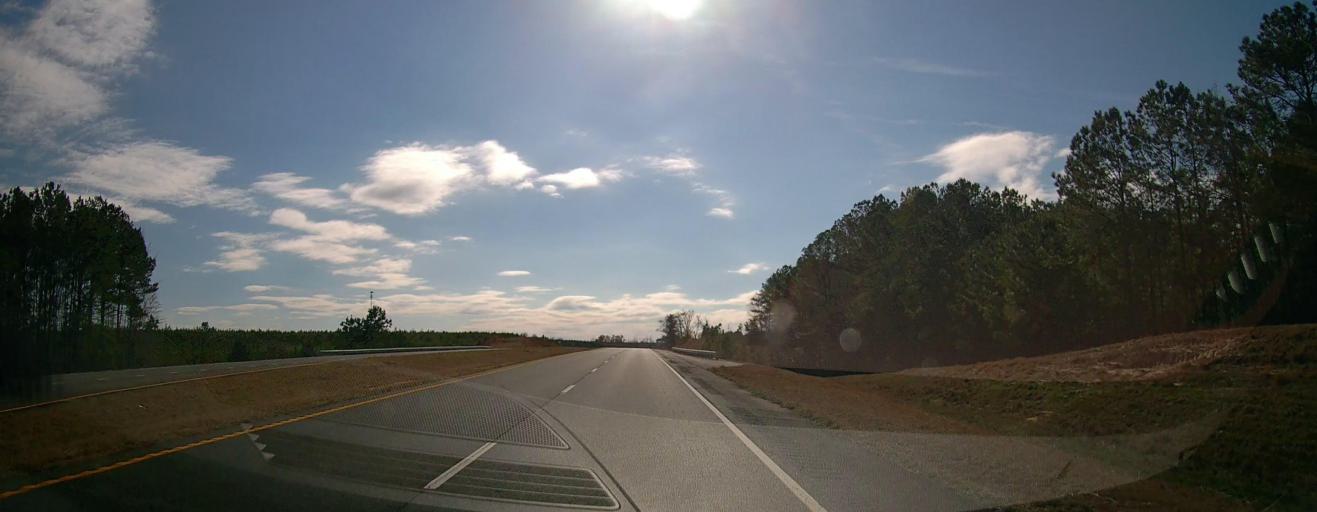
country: US
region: Georgia
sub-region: Taylor County
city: Butler
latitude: 32.4263
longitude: -84.2875
